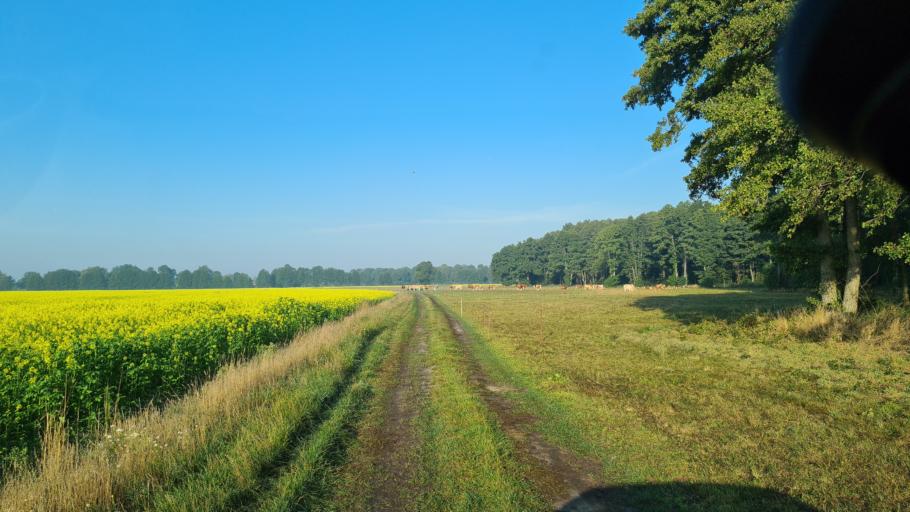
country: DE
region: Brandenburg
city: Schonewalde
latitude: 51.6578
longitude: 13.6125
